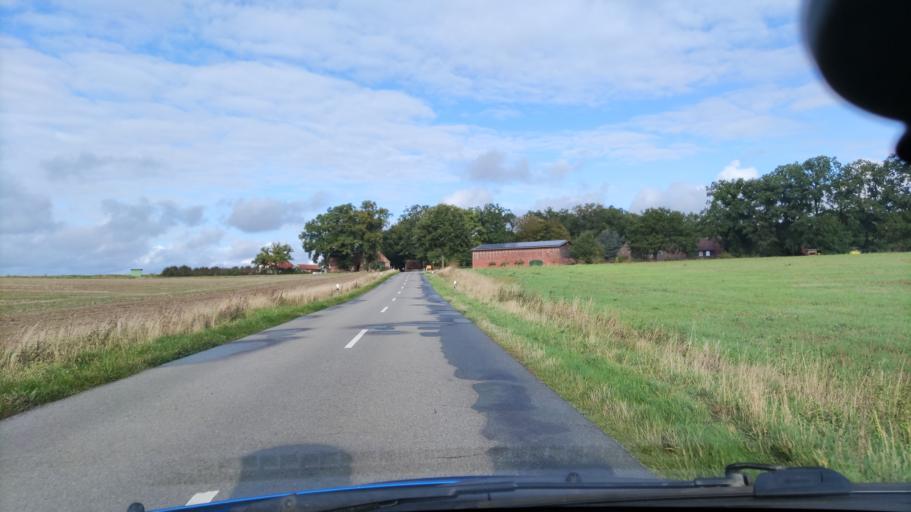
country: DE
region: Lower Saxony
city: Romstedt
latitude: 53.0747
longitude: 10.6706
